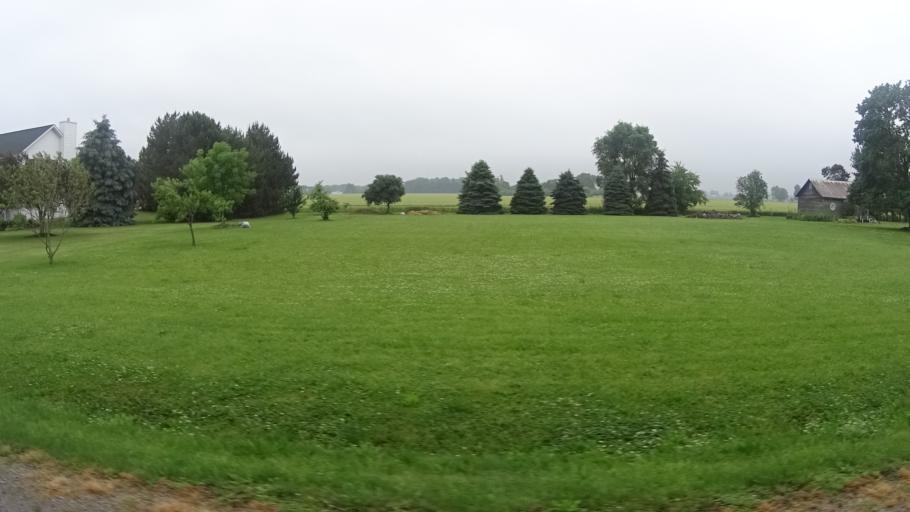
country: US
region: Ohio
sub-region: Huron County
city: Bellevue
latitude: 41.3619
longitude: -82.7904
